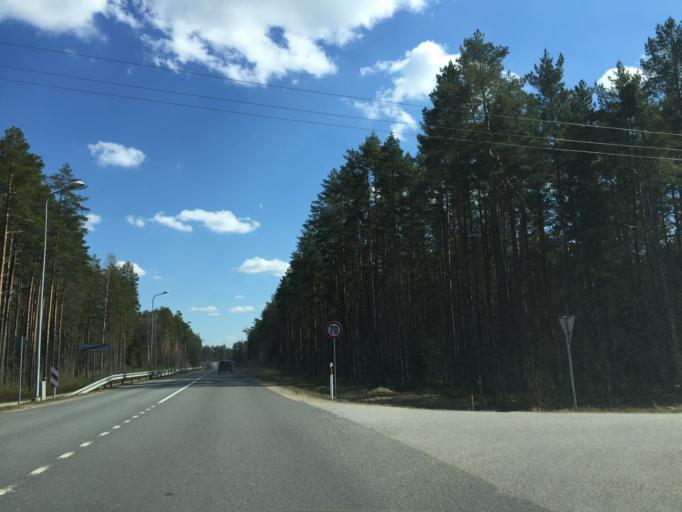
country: LV
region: Saulkrastu
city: Saulkrasti
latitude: 57.2490
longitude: 24.4153
